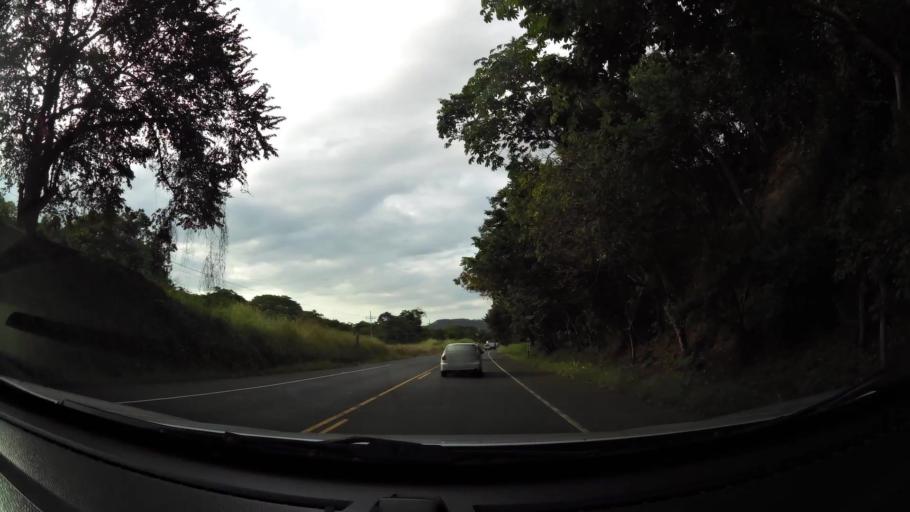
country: CR
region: Puntarenas
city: Esparza
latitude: 9.8974
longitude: -84.6562
